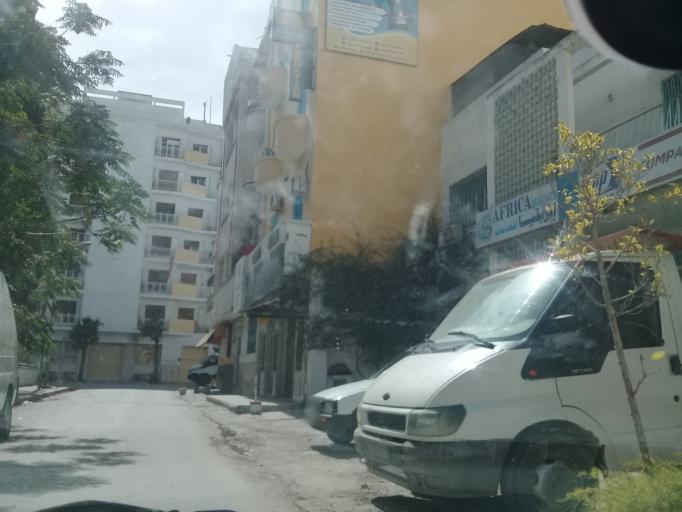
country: TN
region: Tunis
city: Tunis
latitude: 36.8187
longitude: 10.1791
